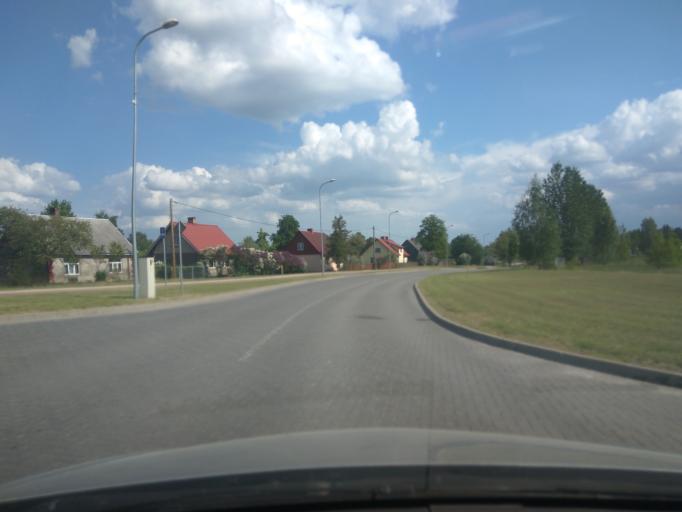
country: LV
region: Kuldigas Rajons
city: Kuldiga
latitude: 56.9799
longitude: 21.9488
